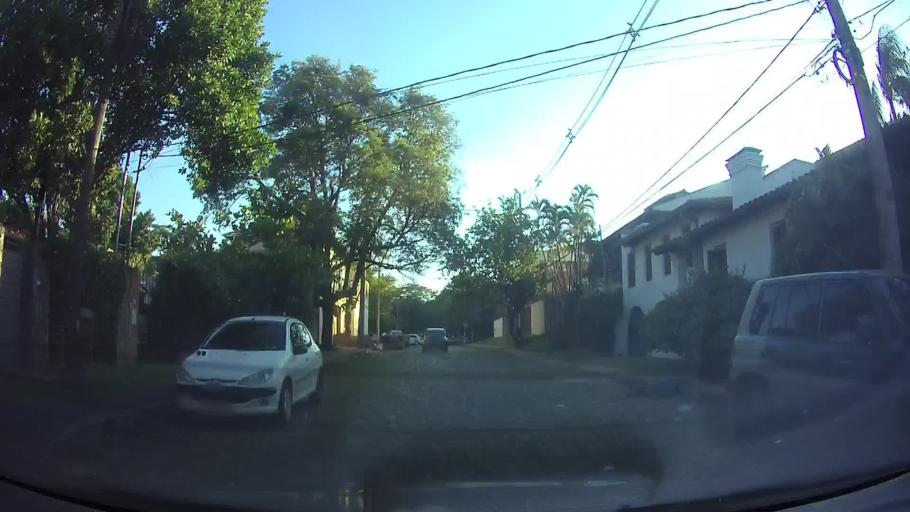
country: PY
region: Asuncion
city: Asuncion
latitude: -25.2816
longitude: -57.5811
